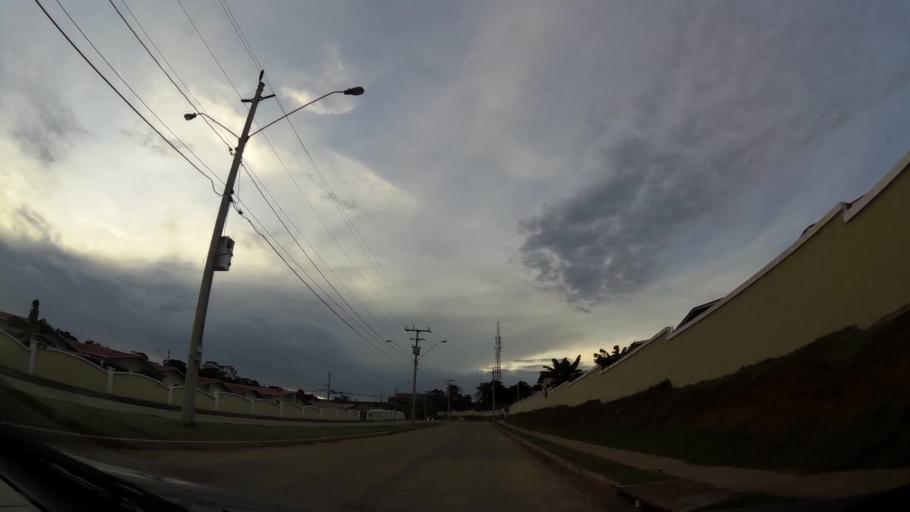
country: PA
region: Panama
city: La Chorrera
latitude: 8.8596
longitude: -79.7638
